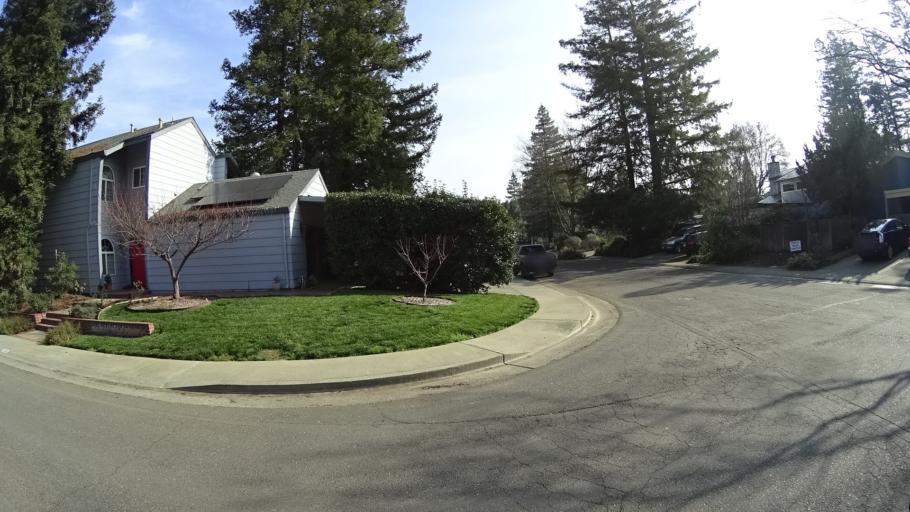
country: US
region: California
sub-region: Yolo County
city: Davis
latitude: 38.5664
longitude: -121.7598
